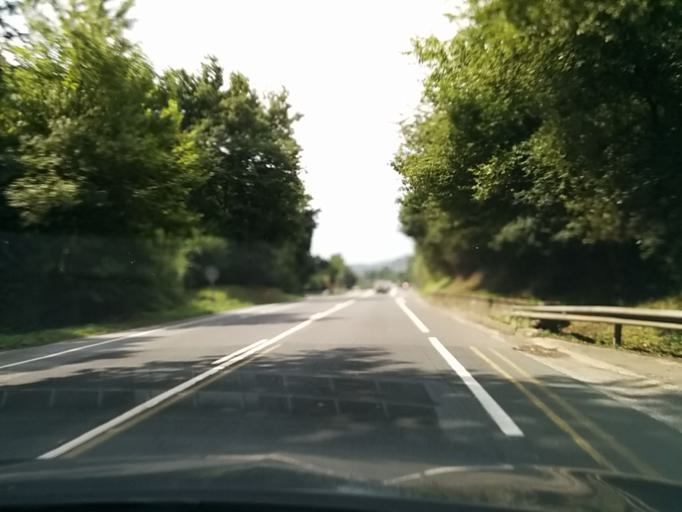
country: ES
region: Basque Country
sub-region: Provincia de Guipuzcoa
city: Lezo
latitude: 43.3225
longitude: -1.8637
